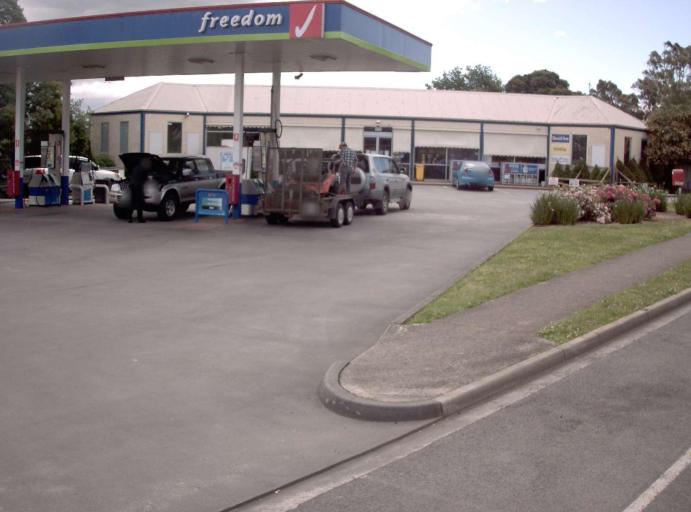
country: AU
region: Victoria
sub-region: Baw Baw
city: Warragul
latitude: -38.1470
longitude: 145.9374
